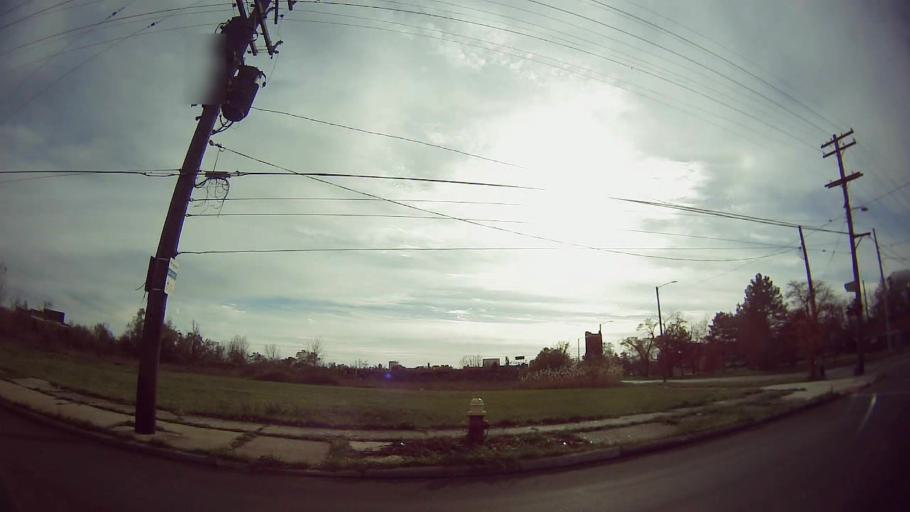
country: US
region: Michigan
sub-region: Wayne County
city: Highland Park
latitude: 42.3760
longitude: -83.1489
